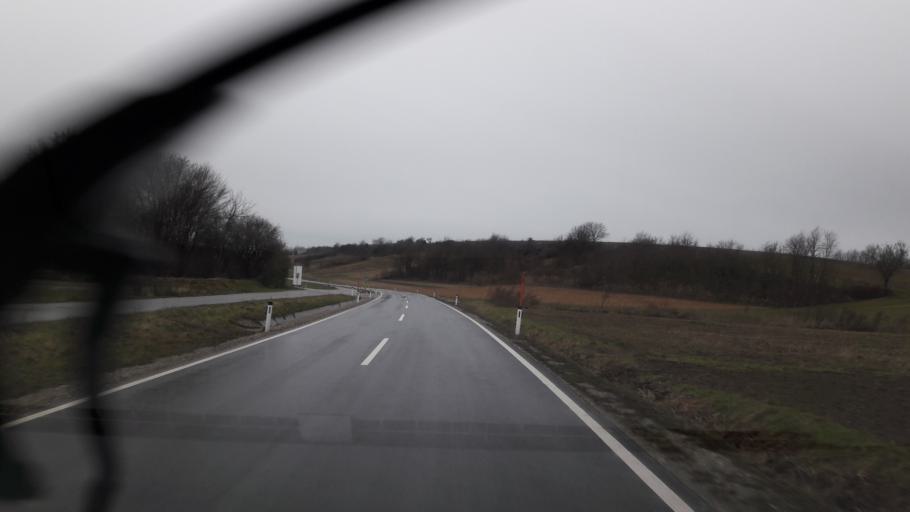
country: AT
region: Lower Austria
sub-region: Politischer Bezirk Mistelbach
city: Hochleithen
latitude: 48.4400
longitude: 16.5404
